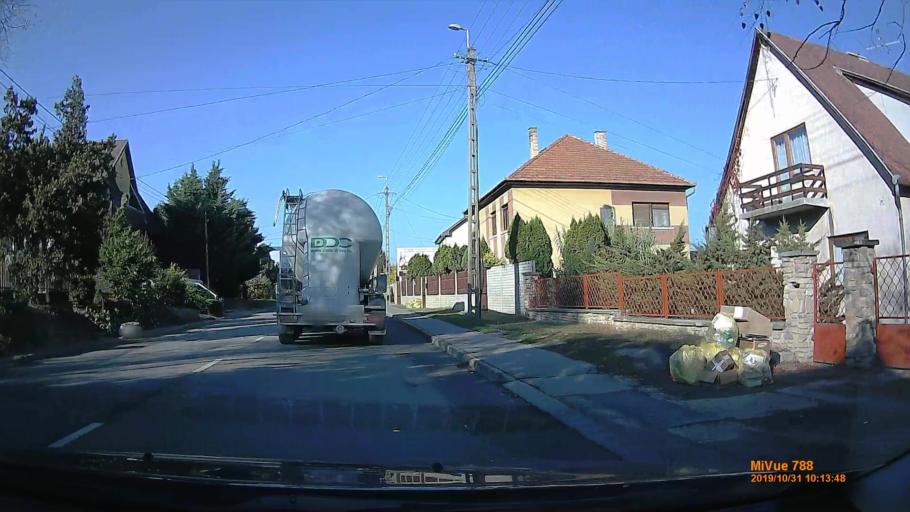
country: HU
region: Pest
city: Pecel
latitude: 47.4914
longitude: 19.3235
